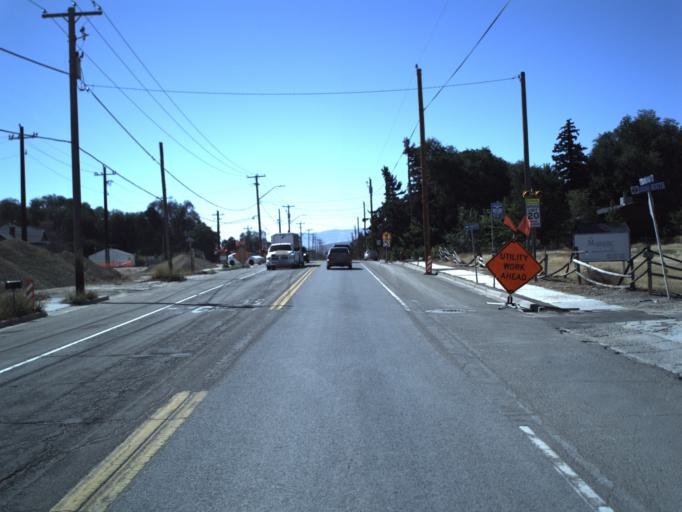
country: US
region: Utah
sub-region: Salt Lake County
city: Riverton
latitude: 40.5124
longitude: -111.9388
